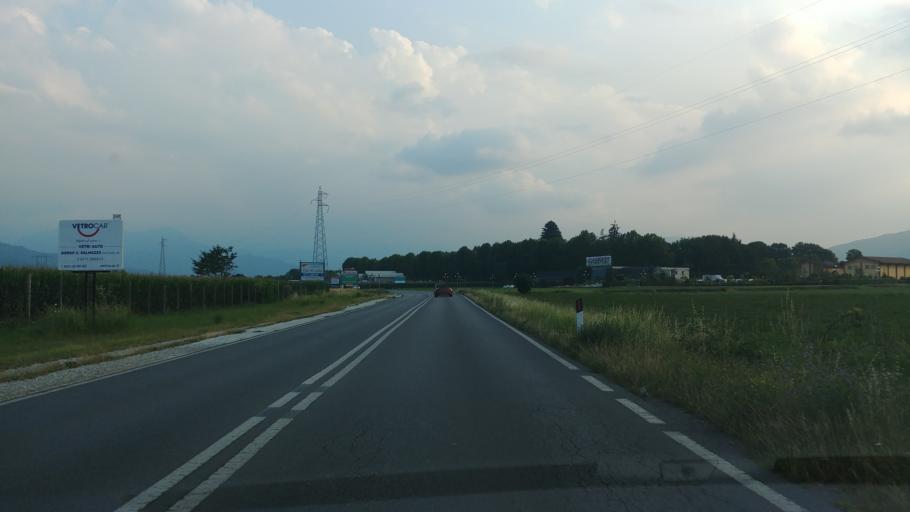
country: IT
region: Piedmont
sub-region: Provincia di Cuneo
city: Cuneo
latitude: 44.3710
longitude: 7.5207
